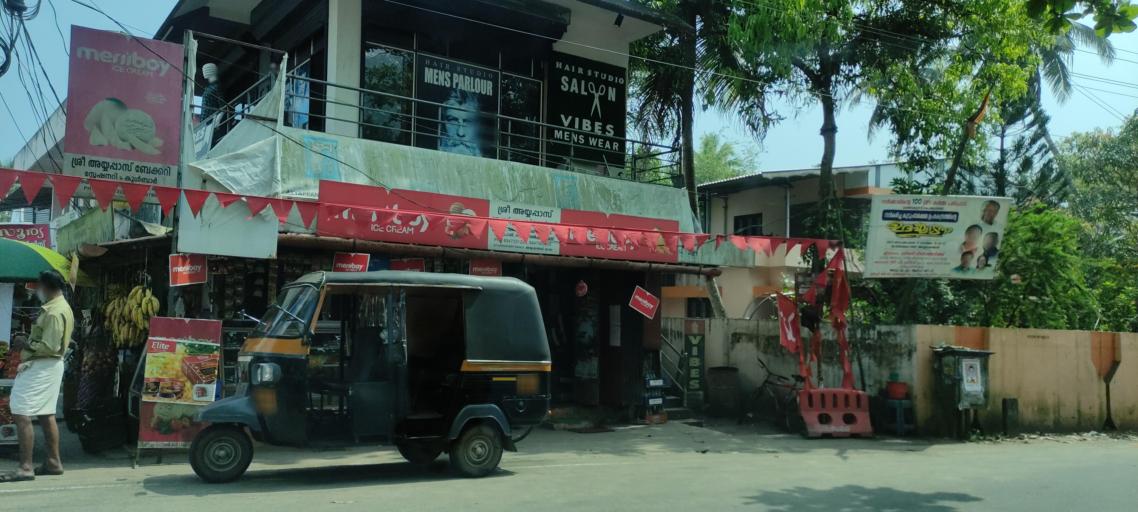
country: IN
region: Kerala
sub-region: Alappuzha
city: Shertallai
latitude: 9.6566
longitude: 76.3587
